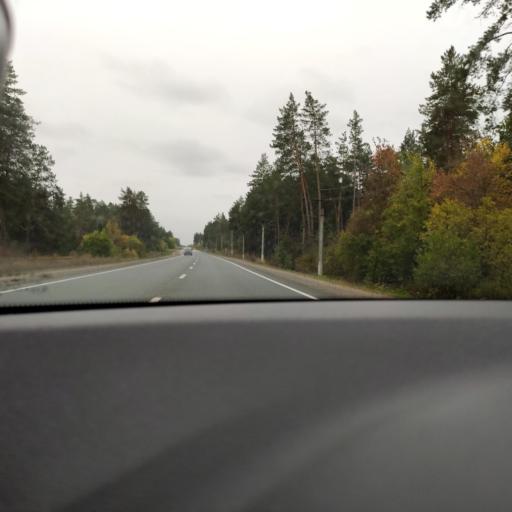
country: RU
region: Samara
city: Mirnyy
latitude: 53.5488
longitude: 50.2956
